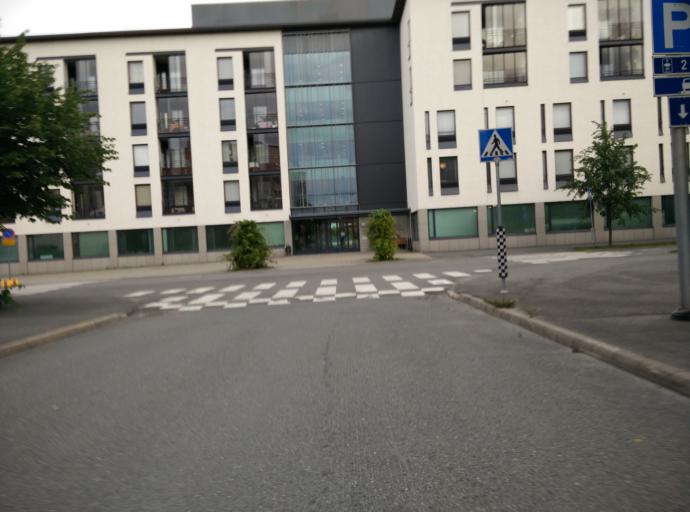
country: FI
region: Haeme
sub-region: Haemeenlinna
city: Haemeenlinna
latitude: 60.9990
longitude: 24.4811
